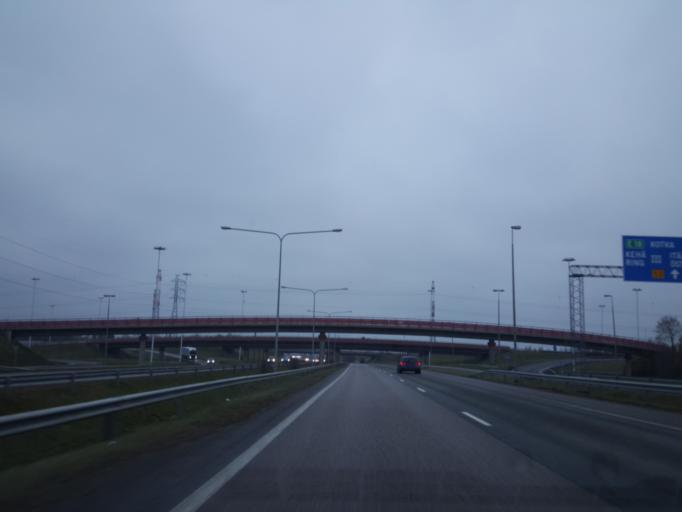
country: FI
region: Uusimaa
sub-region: Helsinki
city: Vantaa
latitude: 60.2919
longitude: 24.9821
